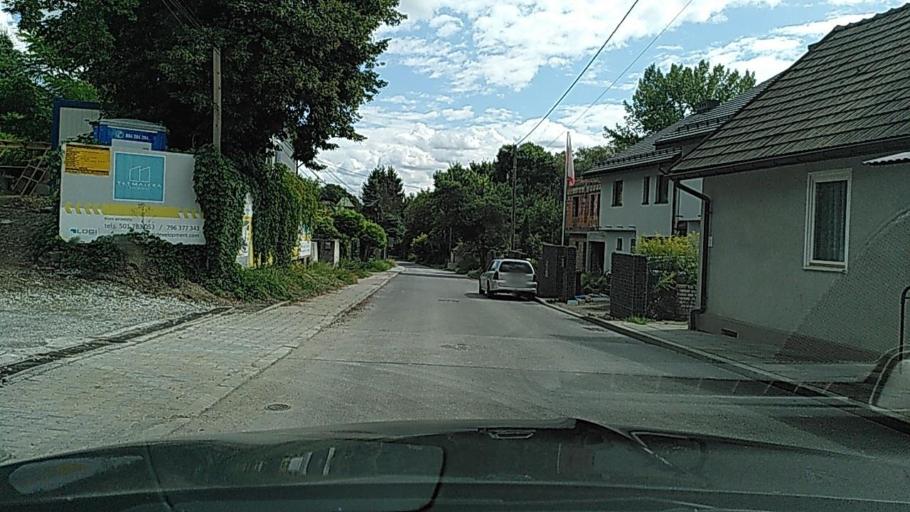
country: PL
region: Lesser Poland Voivodeship
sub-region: Powiat krakowski
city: Rzaska
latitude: 50.0887
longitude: 19.8736
